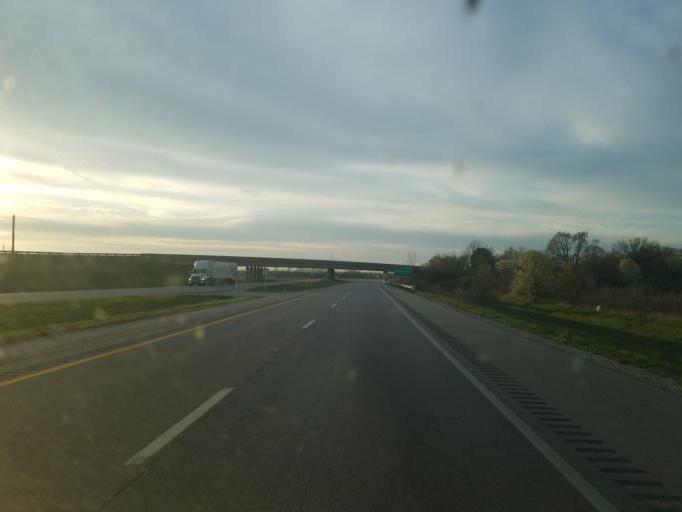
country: US
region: Ohio
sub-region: Wood County
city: Walbridge
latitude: 41.5773
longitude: -83.4721
